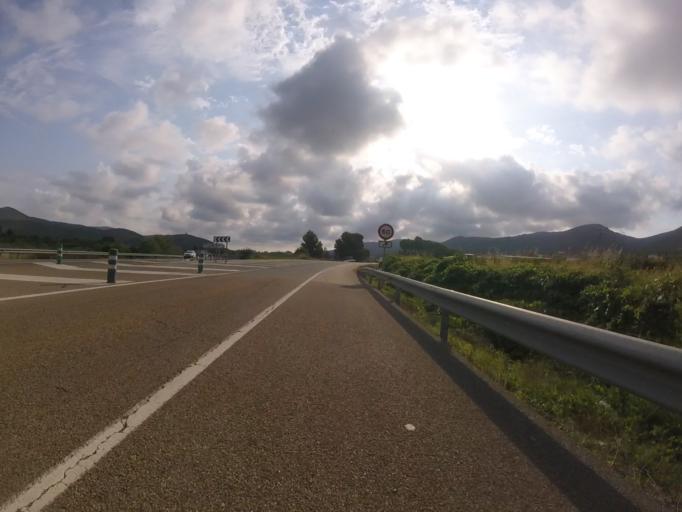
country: ES
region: Valencia
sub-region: Provincia de Castello
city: Santa Magdalena de Pulpis
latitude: 40.3547
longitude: 0.2955
